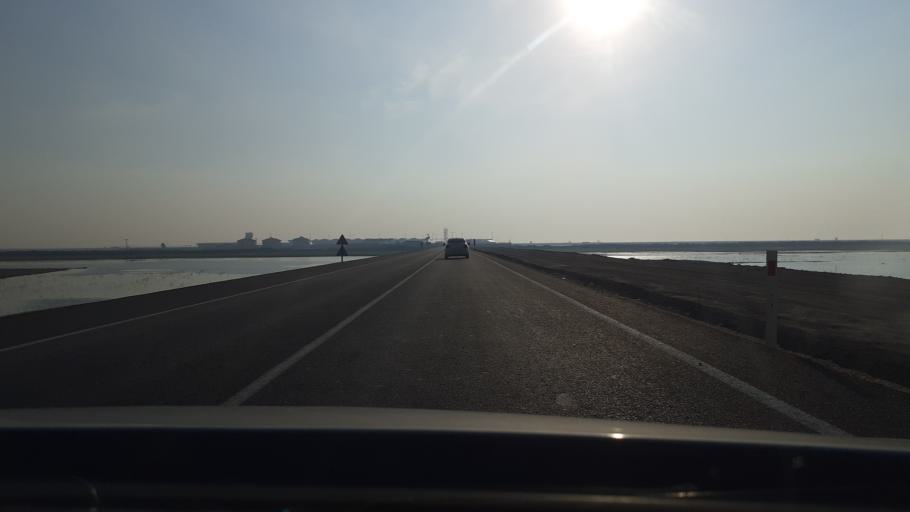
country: TR
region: Hatay
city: Serinyol
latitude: 36.3666
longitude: 36.2661
